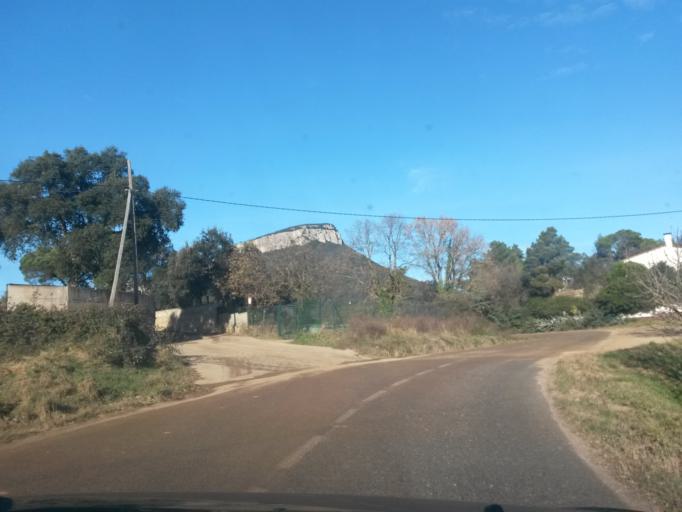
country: ES
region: Catalonia
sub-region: Provincia de Girona
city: la Cellera de Ter
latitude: 42.0070
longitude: 2.6732
